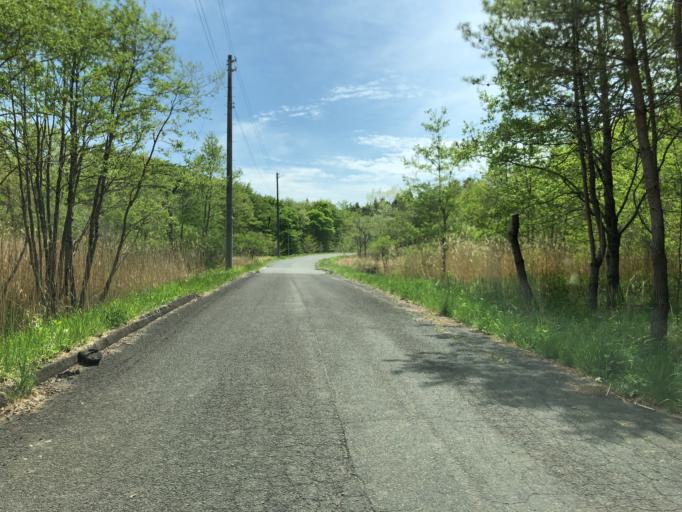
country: JP
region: Miyagi
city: Marumori
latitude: 37.7042
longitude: 140.7788
